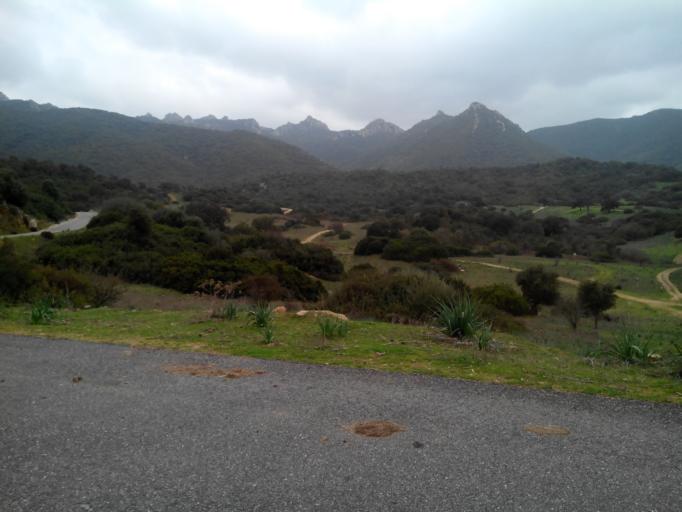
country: IT
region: Sardinia
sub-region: Provincia di Nuoro
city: Austis
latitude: 40.1280
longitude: 9.0319
